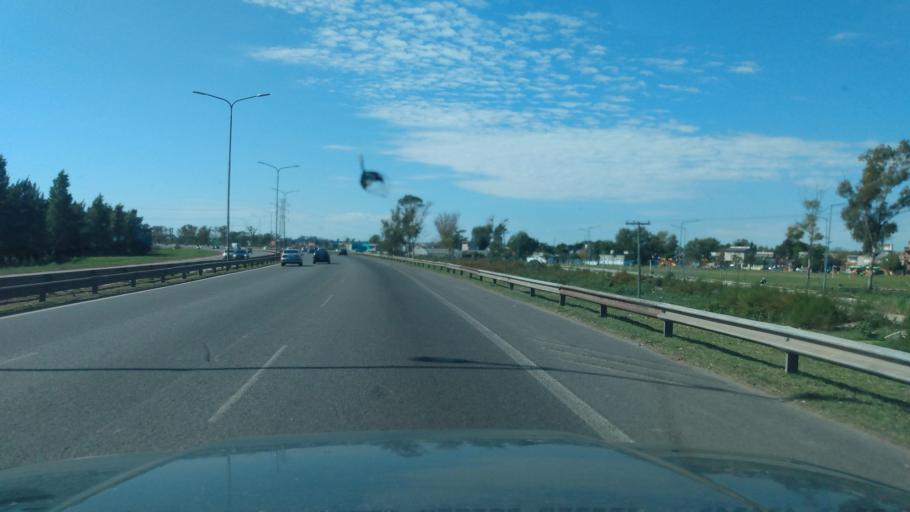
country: AR
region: Buenos Aires
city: Hurlingham
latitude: -34.5515
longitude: -58.6125
